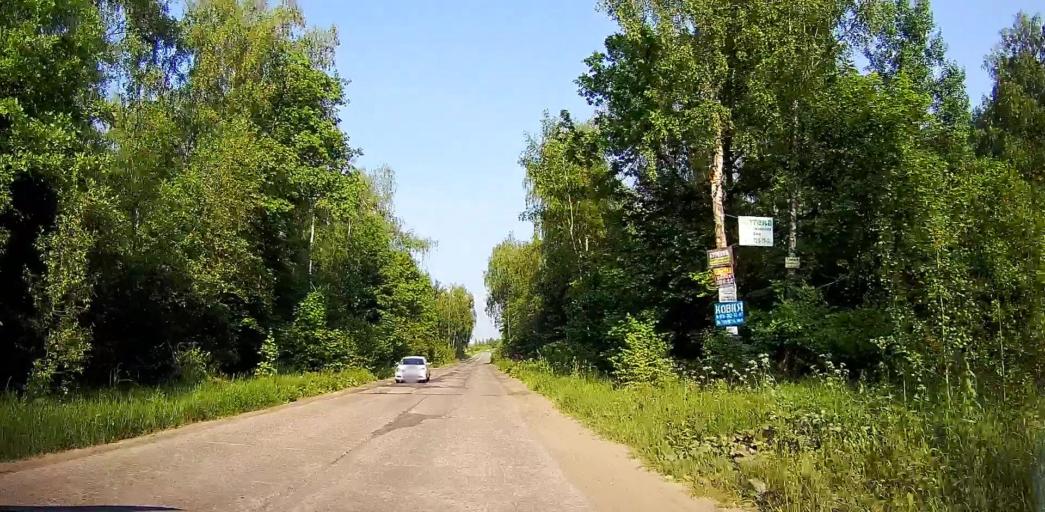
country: RU
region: Moskovskaya
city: Yakovlevskoye
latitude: 55.4314
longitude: 37.9256
